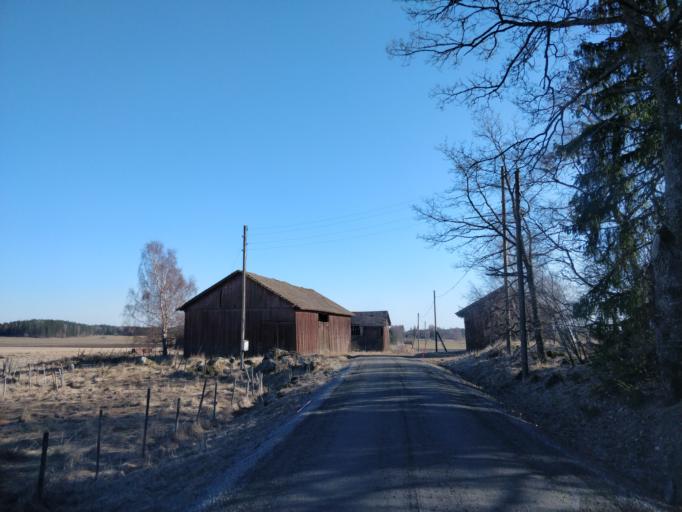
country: SE
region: Uppsala
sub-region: Enkopings Kommun
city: Enkoping
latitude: 59.8211
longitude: 17.1215
